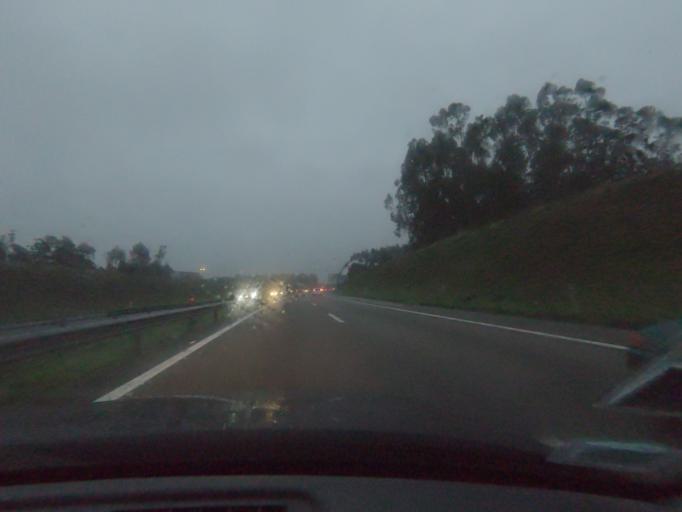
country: PT
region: Porto
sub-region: Matosinhos
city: Santa Cruz do Bispo
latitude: 41.2464
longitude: -8.6950
